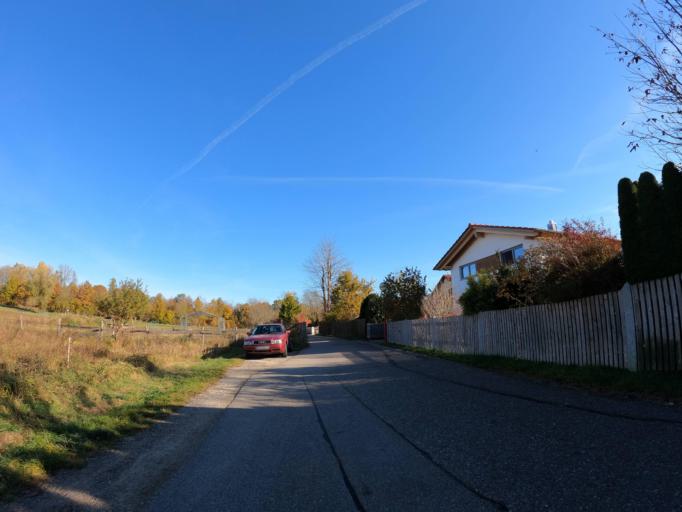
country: DE
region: Bavaria
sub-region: Upper Bavaria
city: Oberhaching
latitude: 48.0320
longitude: 11.5970
